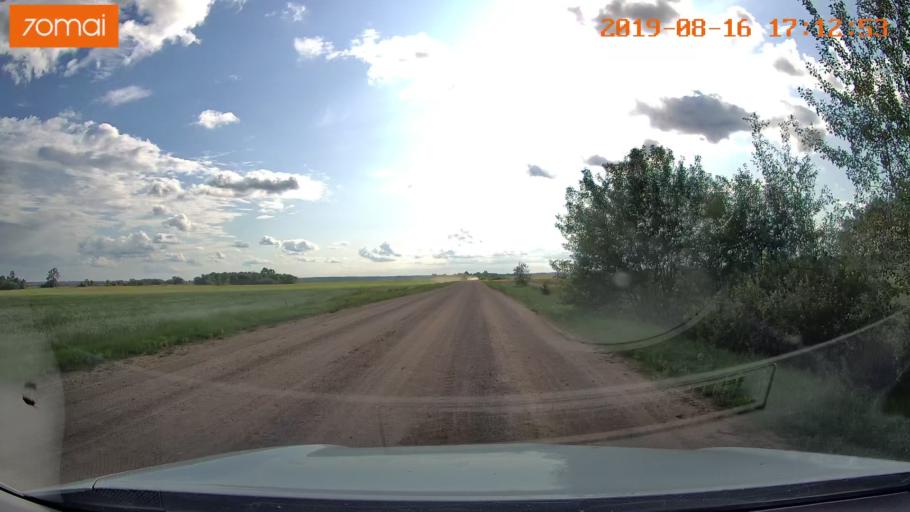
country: BY
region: Mogilev
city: Hlusha
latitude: 53.1927
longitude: 28.8847
